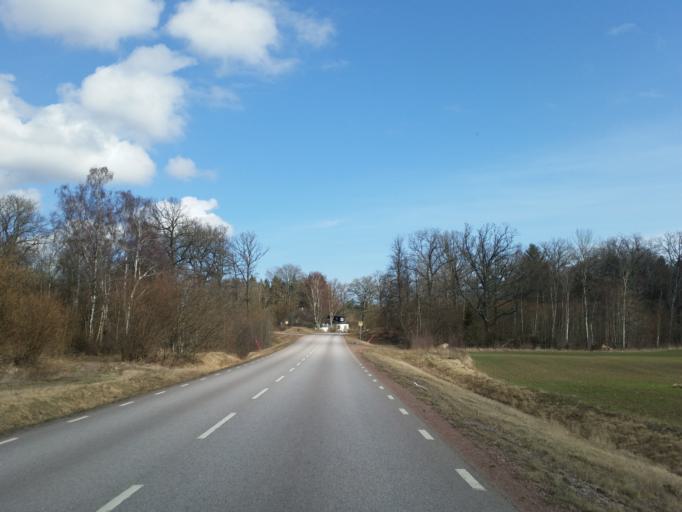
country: SE
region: Kalmar
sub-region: Monsteras Kommun
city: Timmernabben
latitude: 56.8513
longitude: 16.3801
